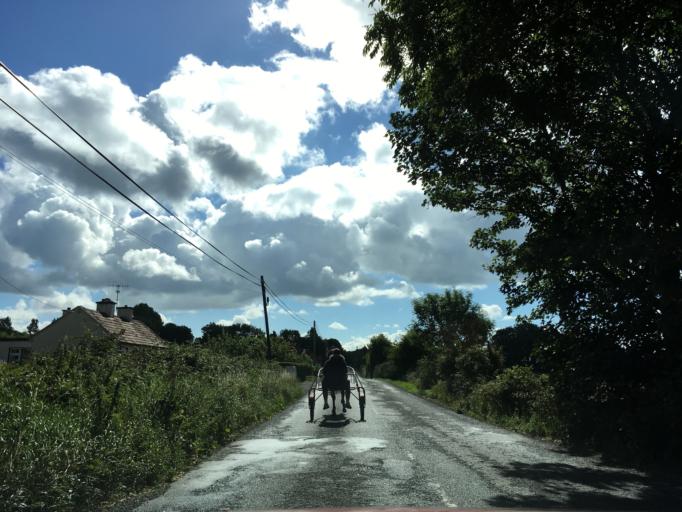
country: IE
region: Munster
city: Cashel
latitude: 52.4445
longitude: -7.8934
